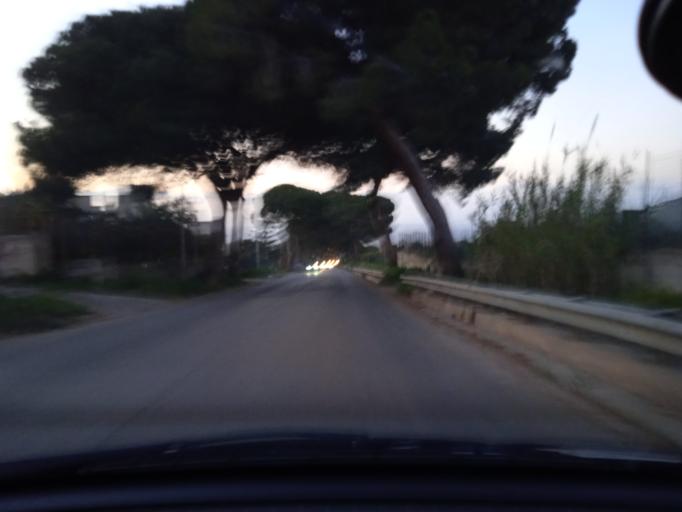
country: IT
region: Sicily
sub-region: Palermo
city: Portella di Mare
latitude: 38.0631
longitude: 13.4599
